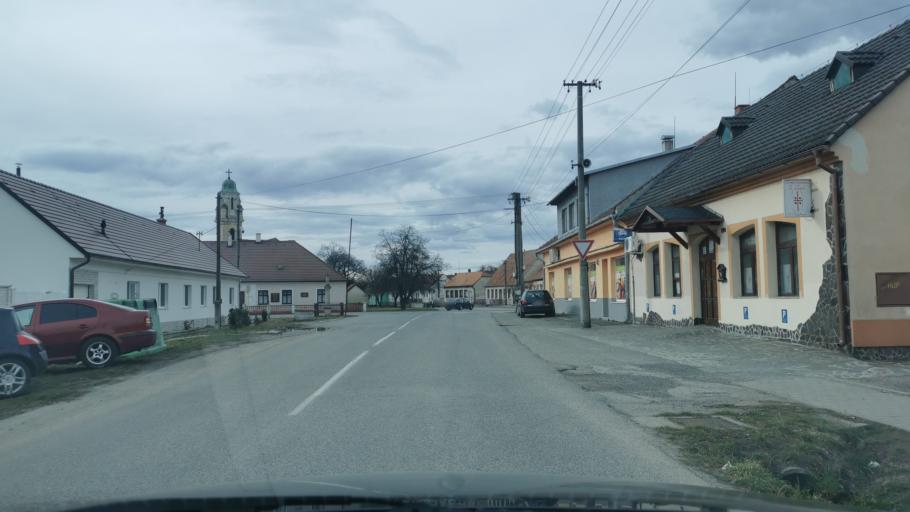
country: CZ
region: South Moravian
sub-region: Okres Breclav
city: Lanzhot
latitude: 48.6909
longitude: 17.0116
